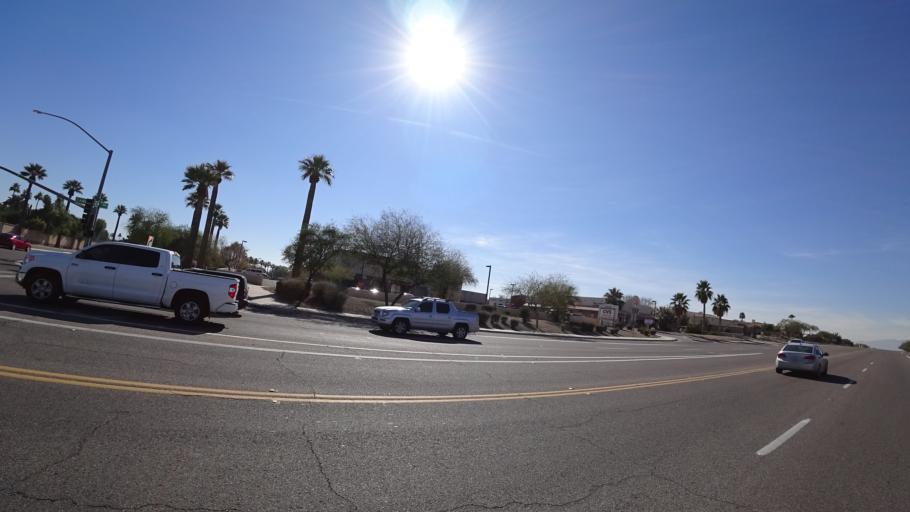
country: US
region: Arizona
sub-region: Maricopa County
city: Litchfield Park
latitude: 33.5083
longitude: -112.3583
